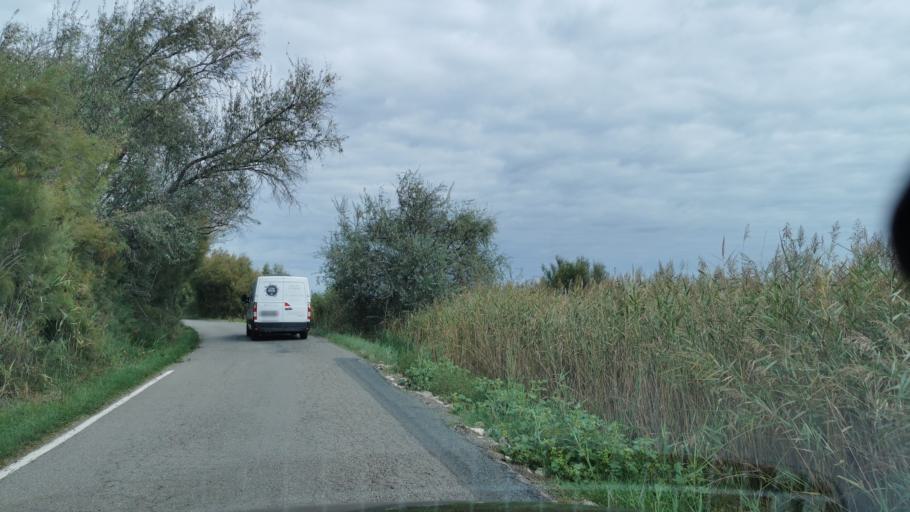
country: FR
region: Languedoc-Roussillon
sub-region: Departement de l'Aude
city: Fleury
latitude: 43.2154
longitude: 3.1946
